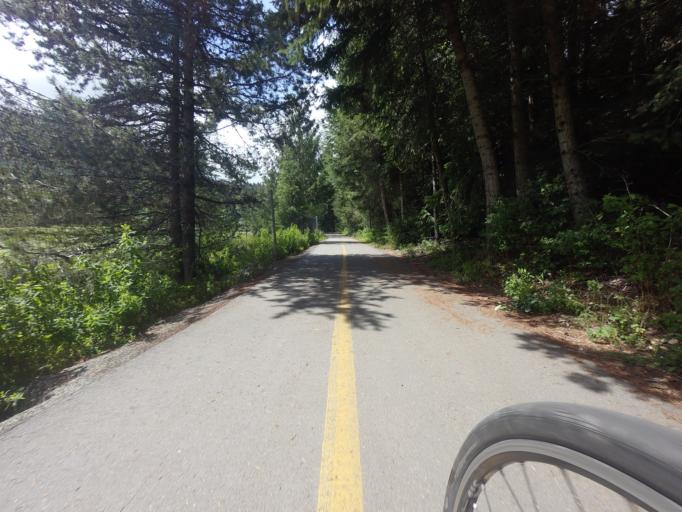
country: CA
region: British Columbia
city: Whistler
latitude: 50.1120
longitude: -122.9675
